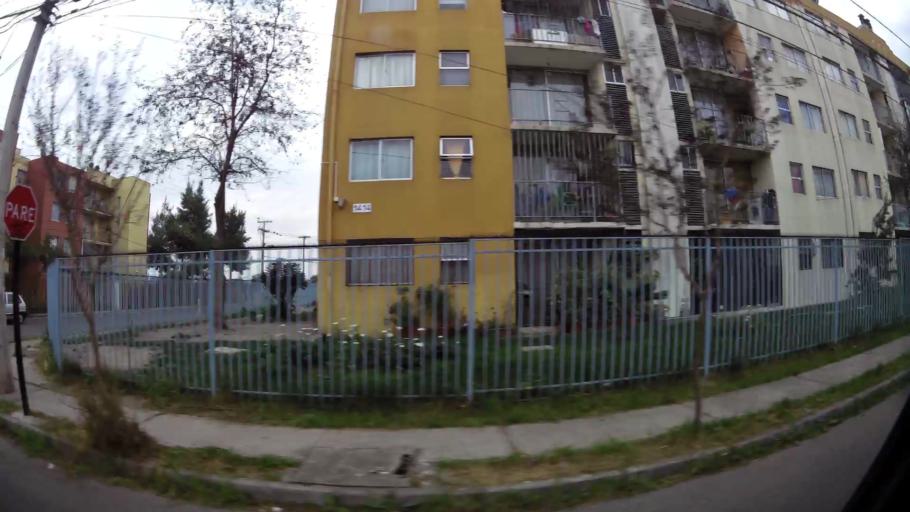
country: CL
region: Santiago Metropolitan
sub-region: Provincia de Santiago
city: Lo Prado
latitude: -33.4858
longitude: -70.7401
